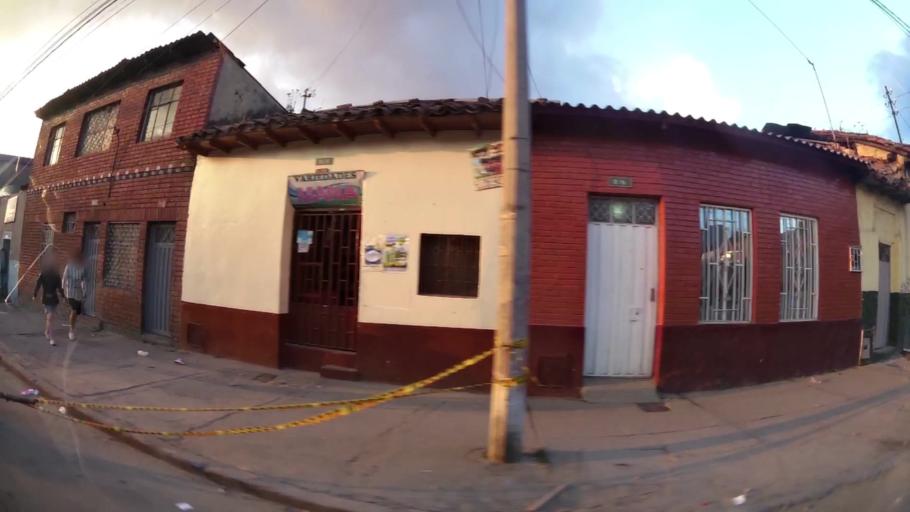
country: CO
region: Bogota D.C.
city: Bogota
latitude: 4.5882
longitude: -74.0826
